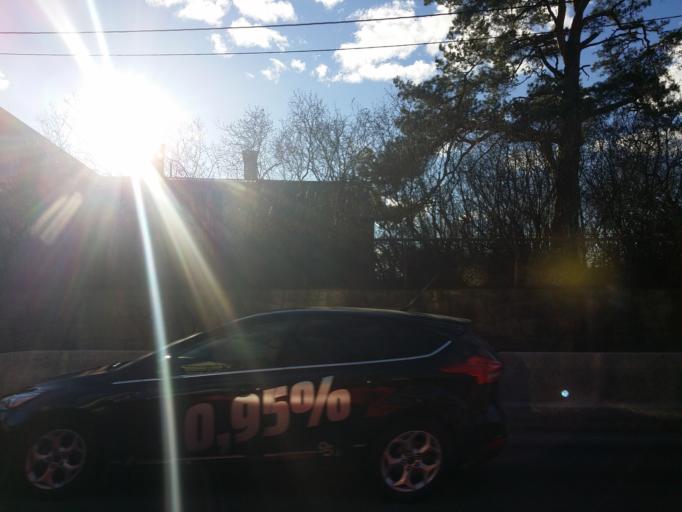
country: NO
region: Akershus
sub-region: Oppegard
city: Kolbotn
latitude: 59.8650
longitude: 10.7838
